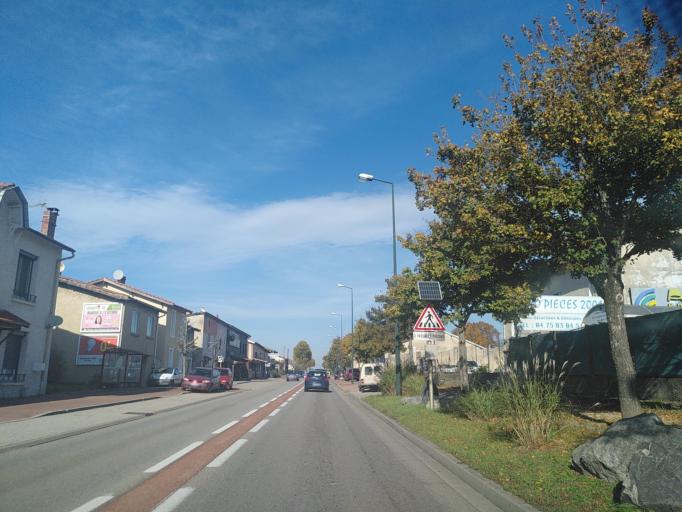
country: FR
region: Rhone-Alpes
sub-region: Departement de la Drome
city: Andancette
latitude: 45.2593
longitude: 4.8233
